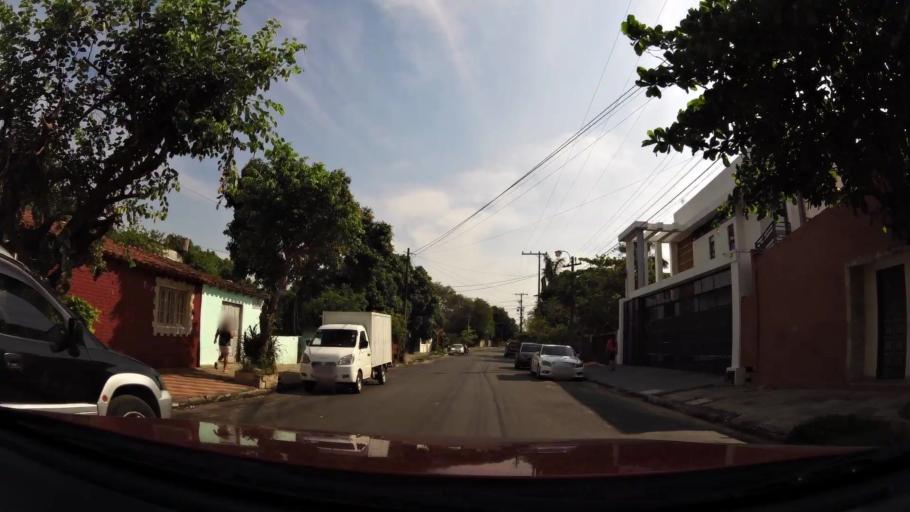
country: PY
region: Central
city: Fernando de la Mora
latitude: -25.2600
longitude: -57.5559
